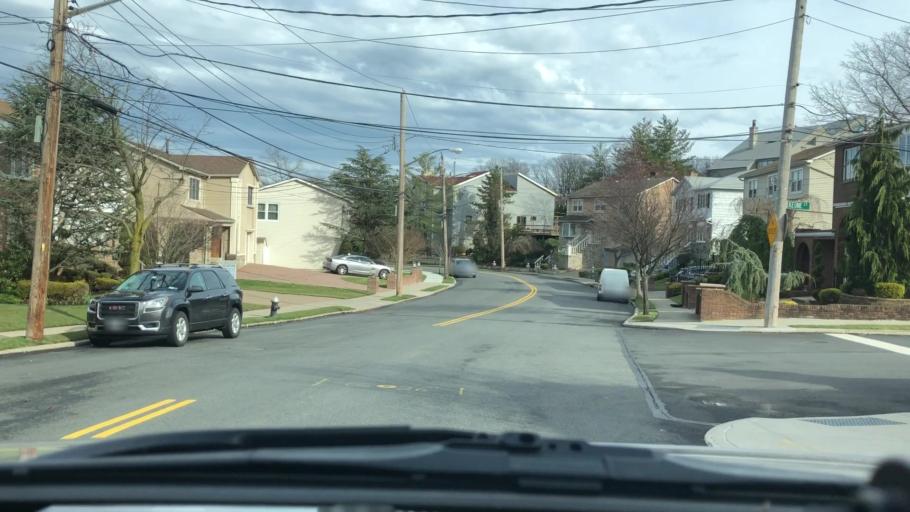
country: US
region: New York
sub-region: Richmond County
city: Staten Island
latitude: 40.6023
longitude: -74.0991
